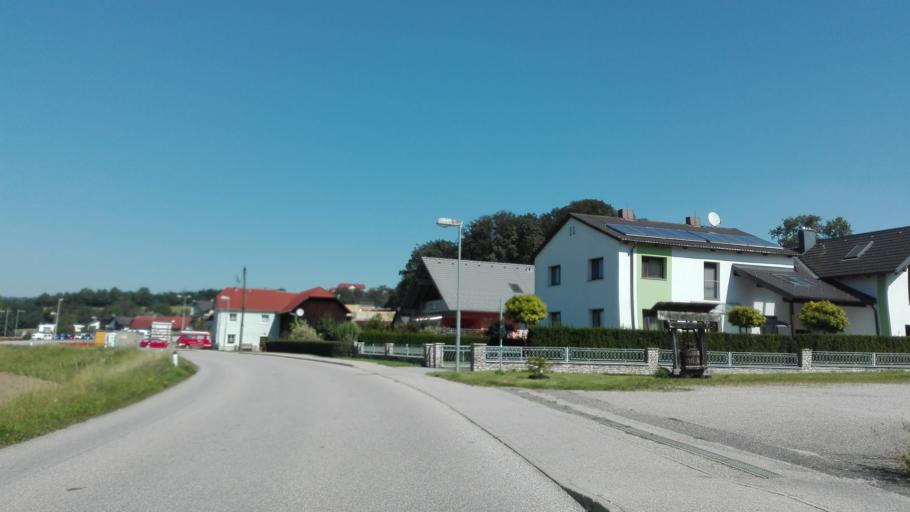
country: AT
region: Upper Austria
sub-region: Politischer Bezirk Perg
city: Bad Kreuzen
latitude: 48.2138
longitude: 14.7436
